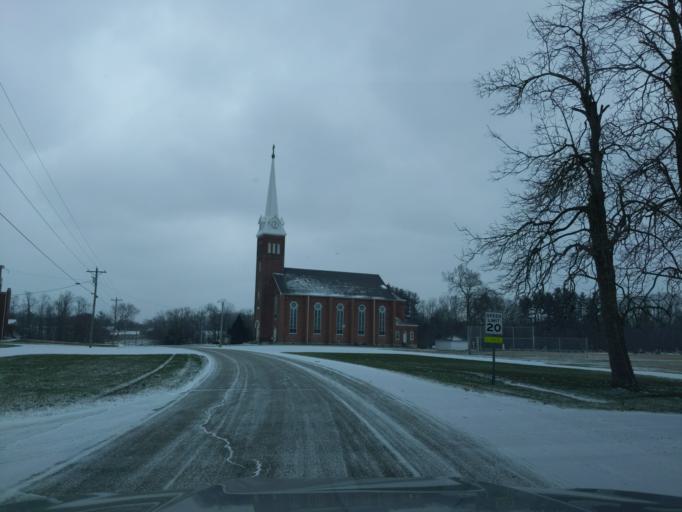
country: US
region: Indiana
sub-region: Decatur County
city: Greensburg
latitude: 39.2114
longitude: -85.4395
